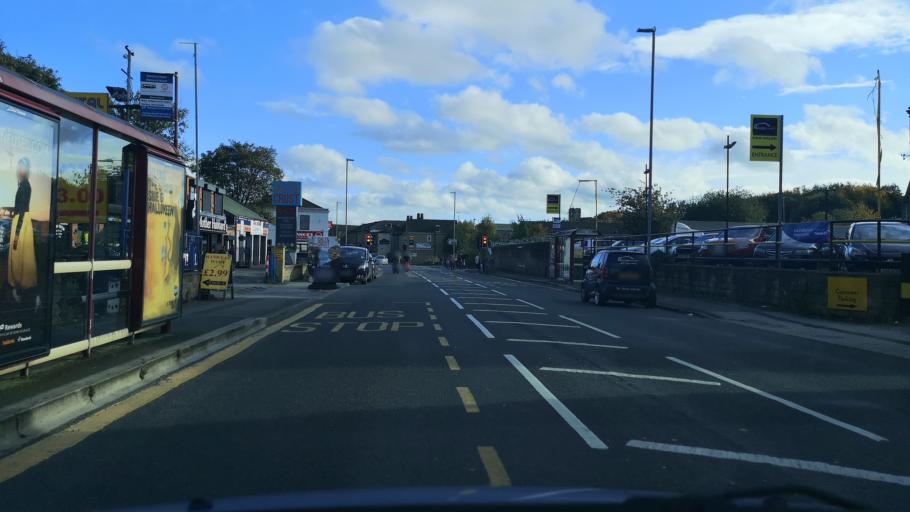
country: GB
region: England
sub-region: Kirklees
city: Batley
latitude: 53.7206
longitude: -1.6436
